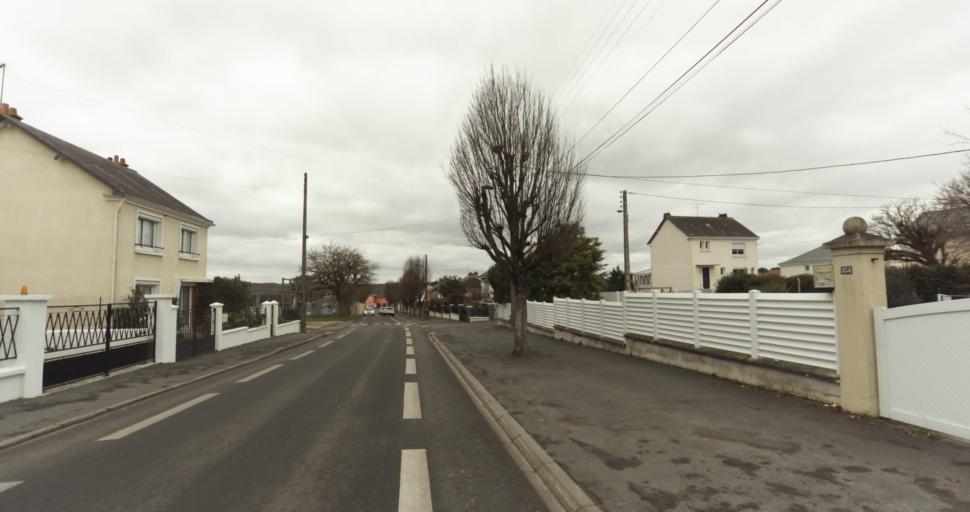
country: FR
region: Pays de la Loire
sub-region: Departement de Maine-et-Loire
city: Varrains
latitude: 47.2446
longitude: -0.0684
